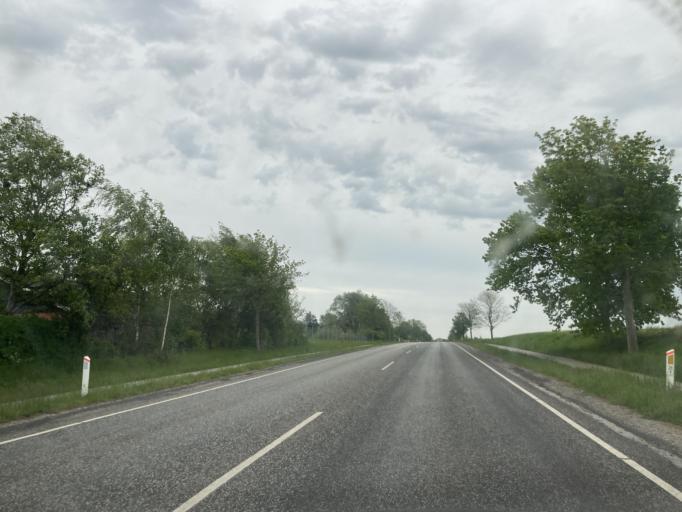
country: DK
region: Zealand
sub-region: Roskilde Kommune
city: Svogerslev
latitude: 55.6321
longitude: 12.0049
